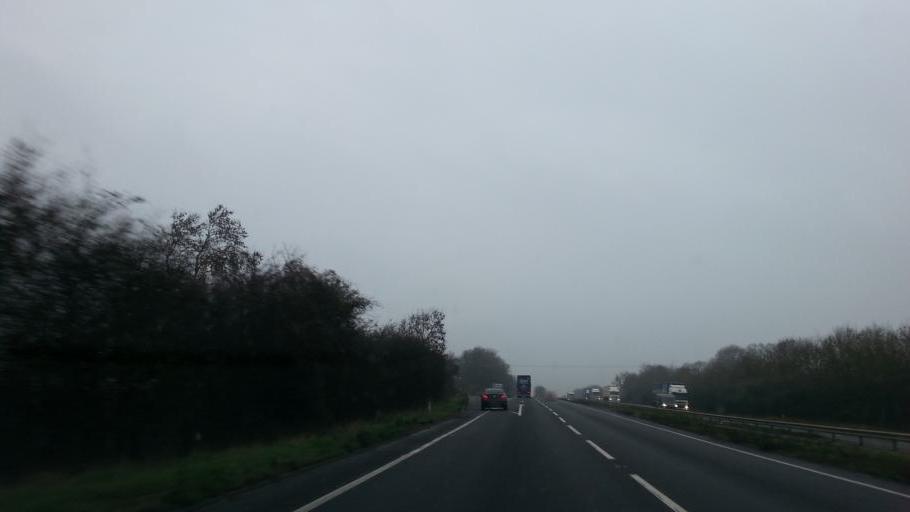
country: GB
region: England
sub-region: District of Rutland
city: Clipsham
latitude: 52.7265
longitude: -0.5975
